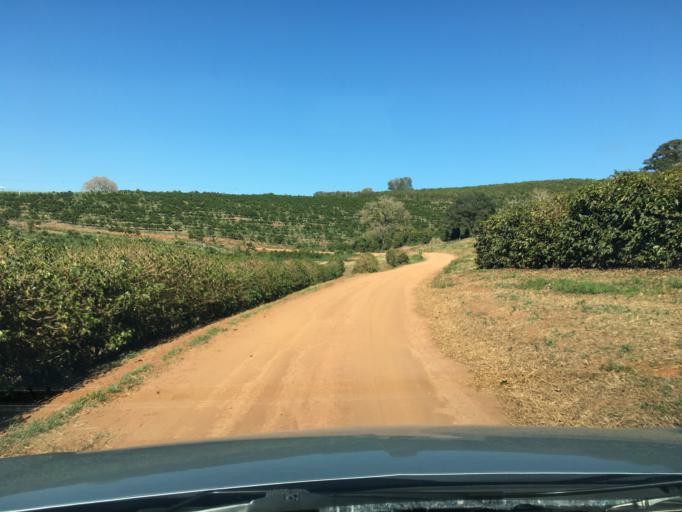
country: BR
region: Minas Gerais
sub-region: Campestre
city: Campestre
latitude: -21.5891
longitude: -46.2075
